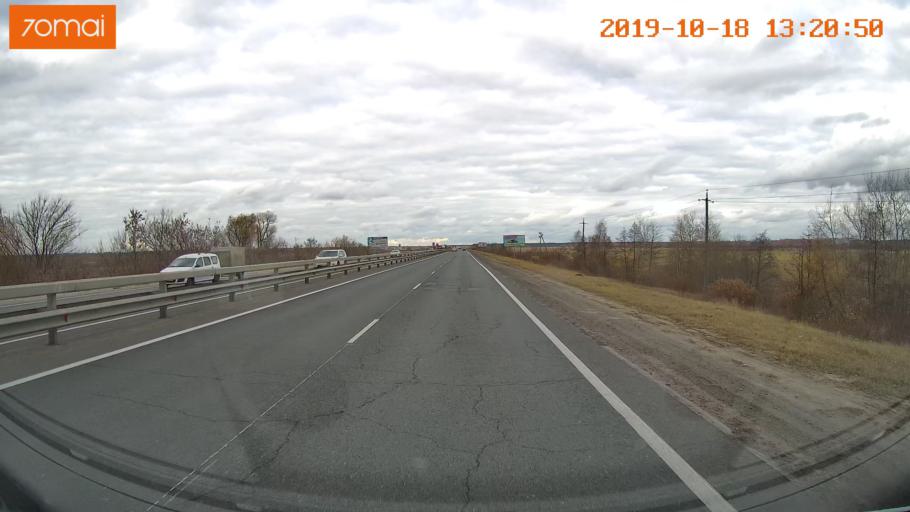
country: RU
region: Rjazan
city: Polyany
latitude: 54.6867
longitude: 39.8350
